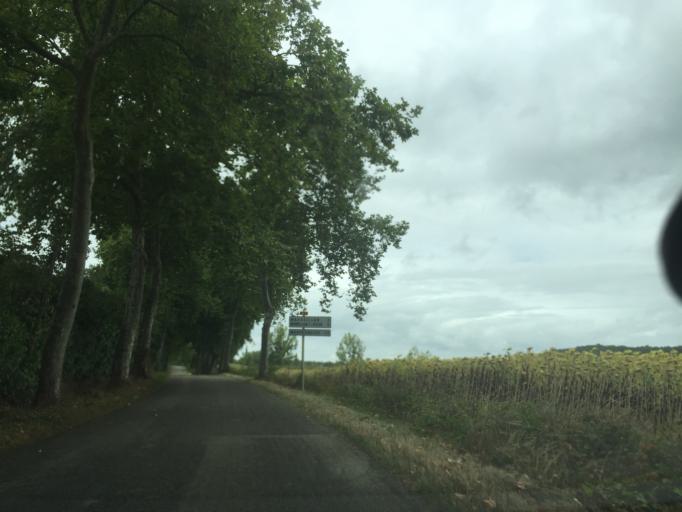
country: FR
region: Midi-Pyrenees
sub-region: Departement du Gers
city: Mielan
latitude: 43.4731
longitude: 0.3268
